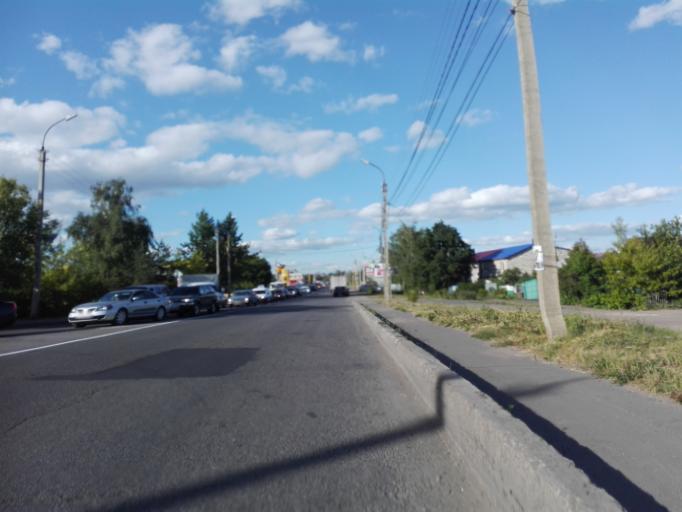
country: RU
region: Orjol
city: Orel
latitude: 52.9400
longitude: 36.0691
